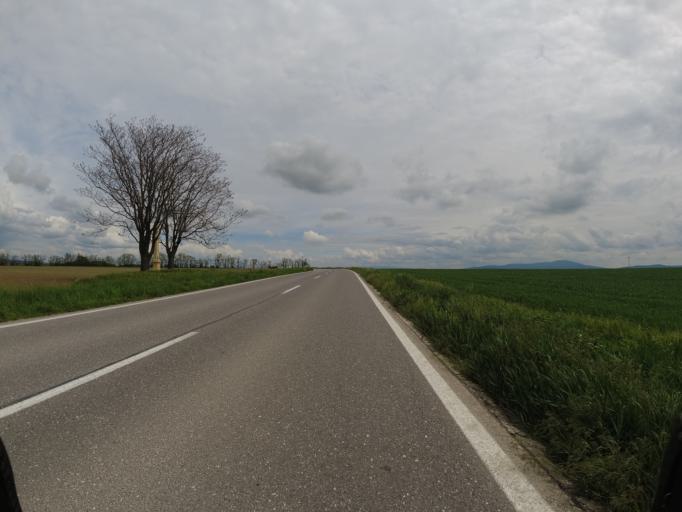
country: SK
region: Trnavsky
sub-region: Okres Trnava
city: Piestany
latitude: 48.5162
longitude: 18.0268
